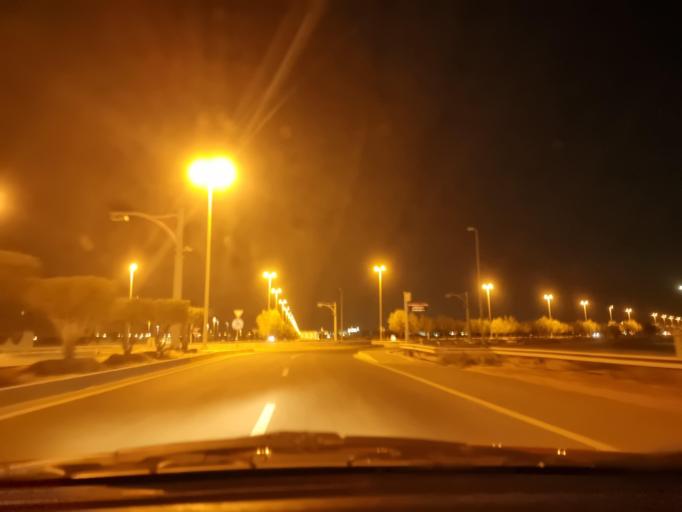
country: AE
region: Abu Dhabi
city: Abu Dhabi
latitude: 24.3741
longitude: 54.6978
